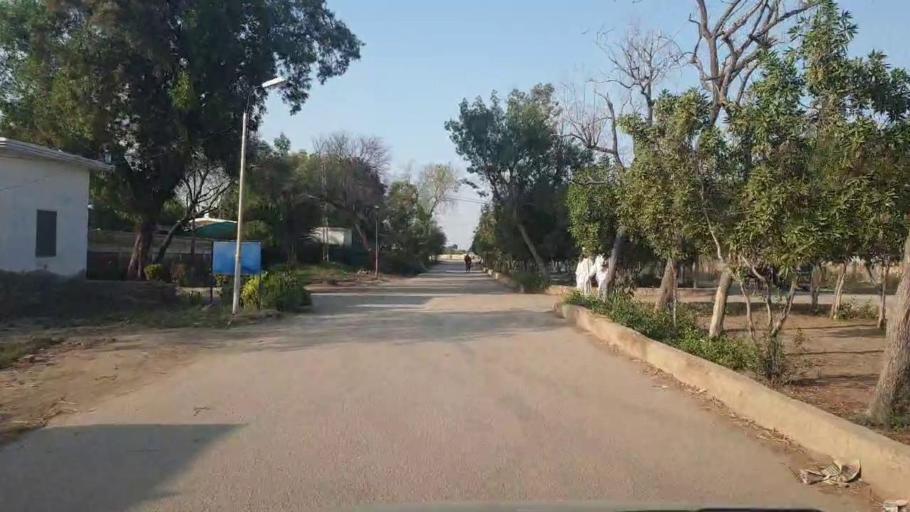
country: PK
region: Sindh
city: Badin
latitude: 24.6548
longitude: 68.8272
